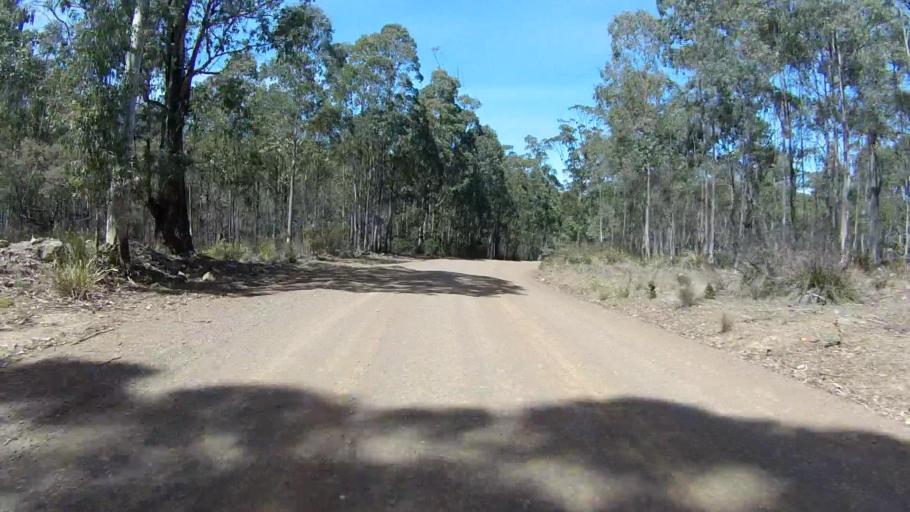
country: AU
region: Tasmania
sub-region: Sorell
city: Sorell
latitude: -42.6694
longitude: 147.7299
